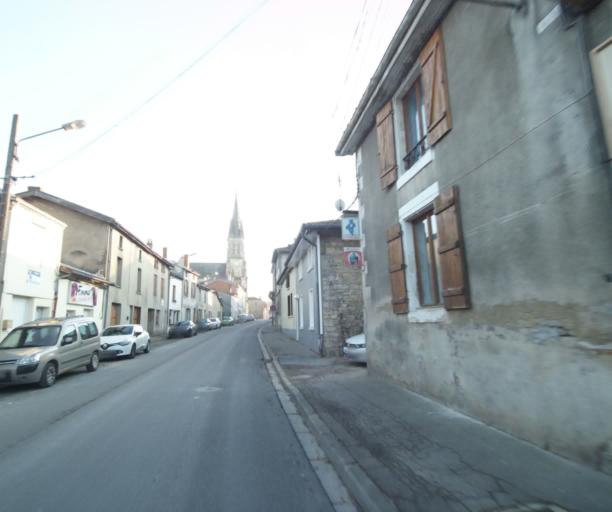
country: FR
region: Champagne-Ardenne
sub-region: Departement de la Haute-Marne
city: Bienville
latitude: 48.5863
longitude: 5.0369
